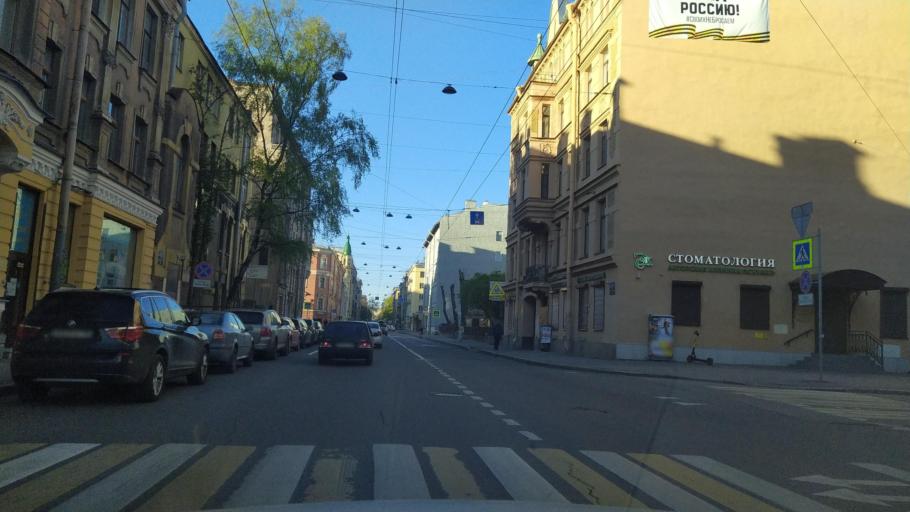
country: RU
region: St.-Petersburg
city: Petrogradka
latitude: 59.9584
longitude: 30.3030
